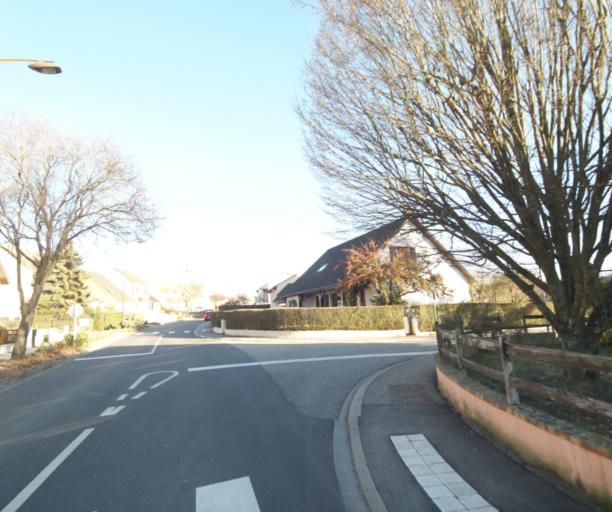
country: FR
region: Lorraine
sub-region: Departement de Meurthe-et-Moselle
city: Seichamps
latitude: 48.7081
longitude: 6.2598
